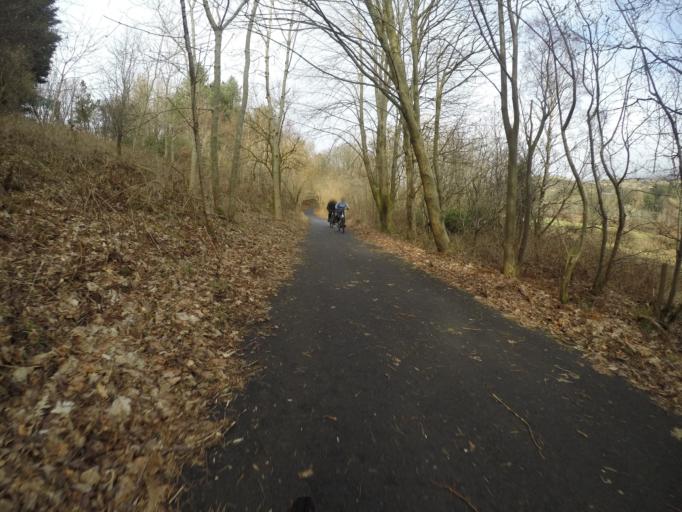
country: GB
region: Scotland
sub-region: North Ayrshire
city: Fairlie
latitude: 55.7388
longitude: -4.8616
